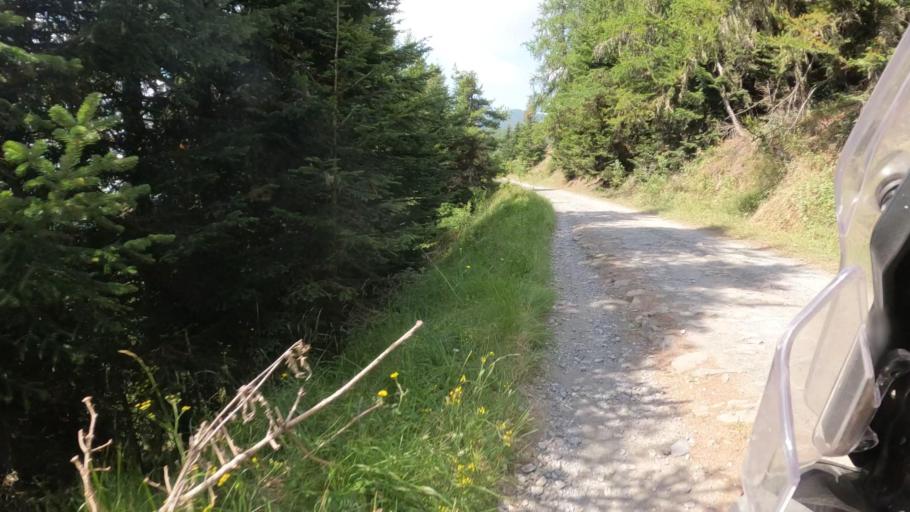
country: IT
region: Piedmont
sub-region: Provincia di Cuneo
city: Briga Alta
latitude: 44.0347
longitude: 7.6808
